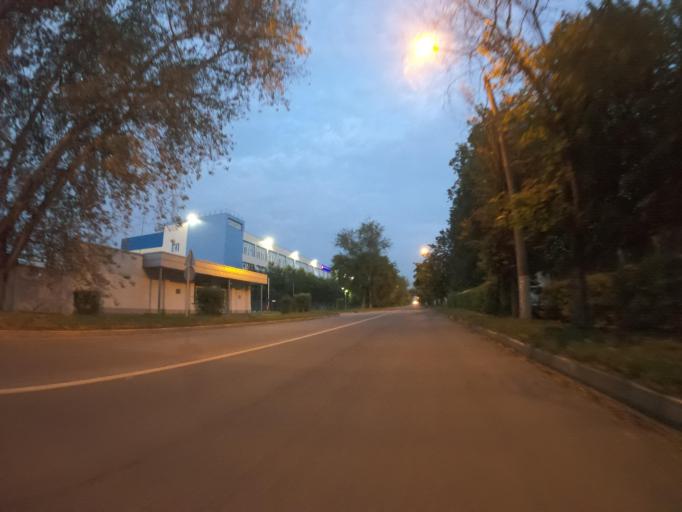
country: RU
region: Moskovskaya
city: Zhukovskiy
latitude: 55.6055
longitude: 38.1175
